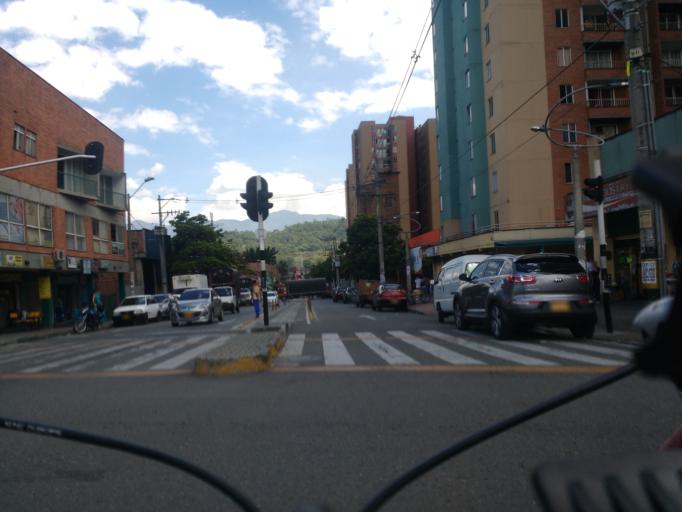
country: CO
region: Antioquia
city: Medellin
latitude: 6.2631
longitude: -75.5683
